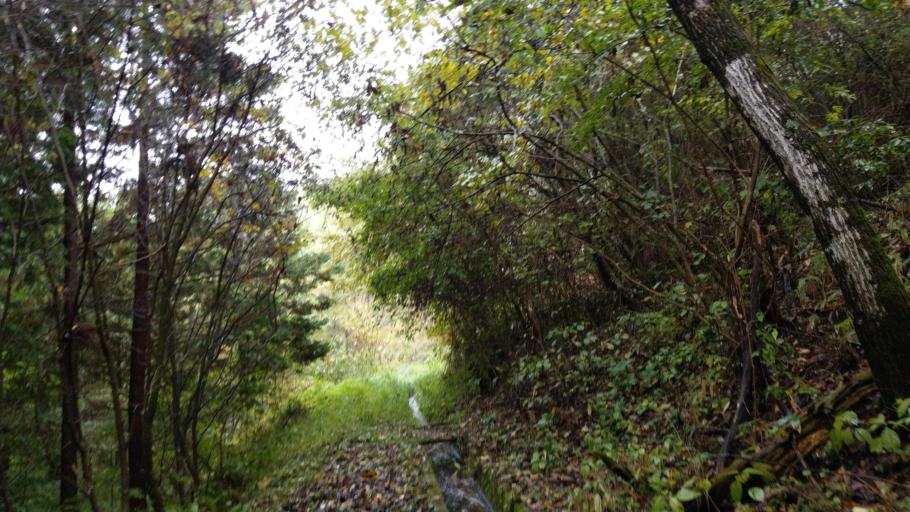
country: JP
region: Nagano
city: Komoro
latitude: 36.3670
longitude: 138.4485
